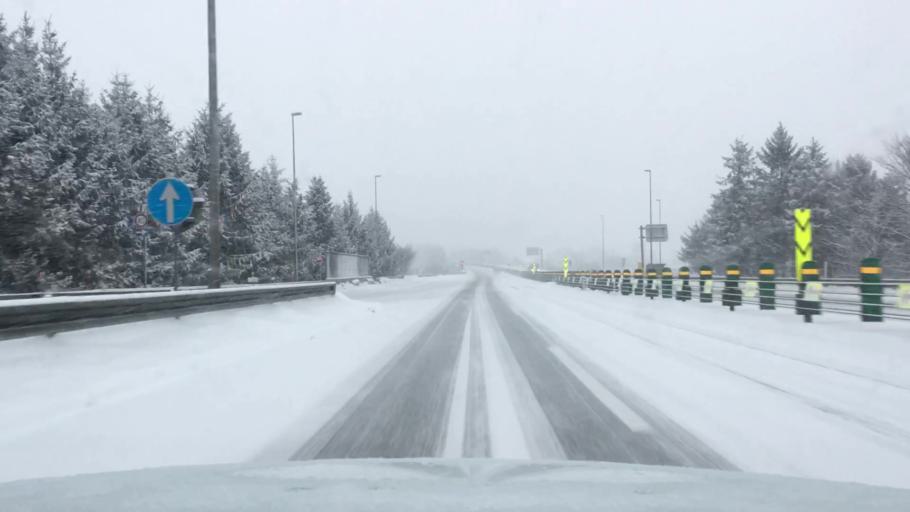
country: JP
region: Akita
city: Hanawa
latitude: 40.2565
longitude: 140.7664
